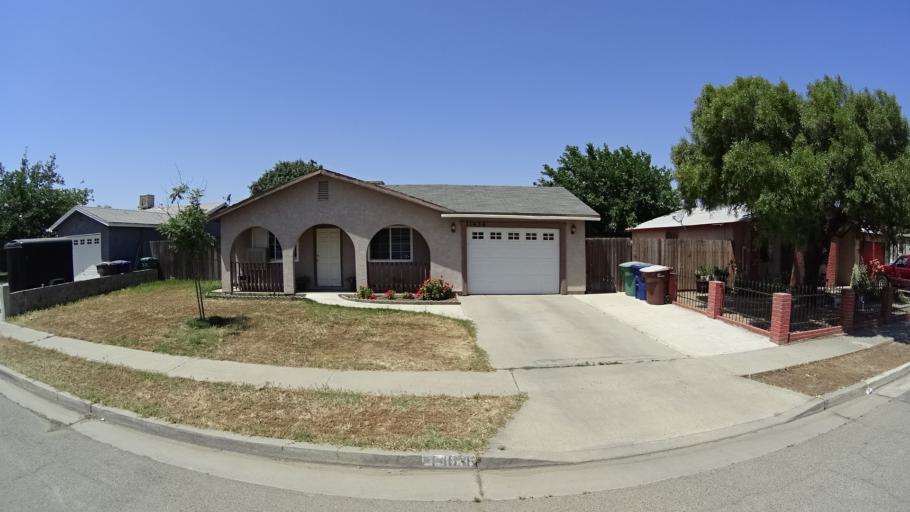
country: US
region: California
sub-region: Kings County
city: Armona
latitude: 36.3068
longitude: -119.7106
